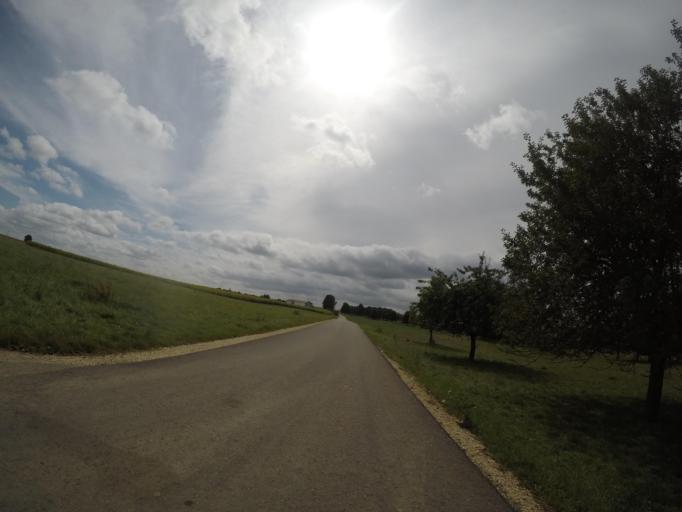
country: DE
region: Baden-Wuerttemberg
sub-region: Tuebingen Region
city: Schelklingen
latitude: 48.4255
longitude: 9.7276
